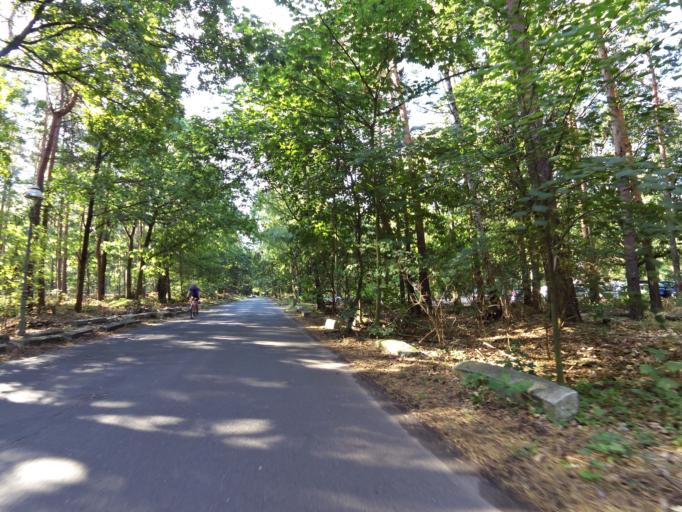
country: DE
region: Berlin
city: Nikolassee
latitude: 52.4392
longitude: 13.1815
